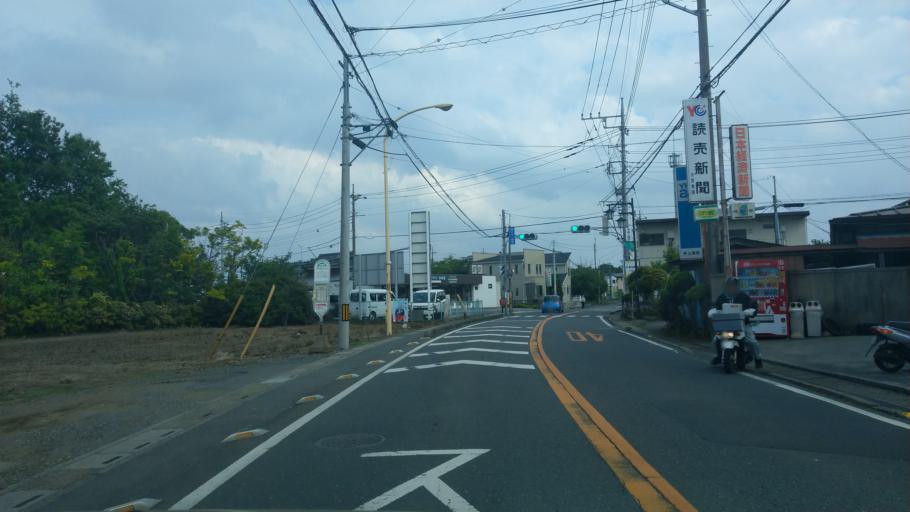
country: JP
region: Saitama
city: Saitama
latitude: 35.9091
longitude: 139.6743
